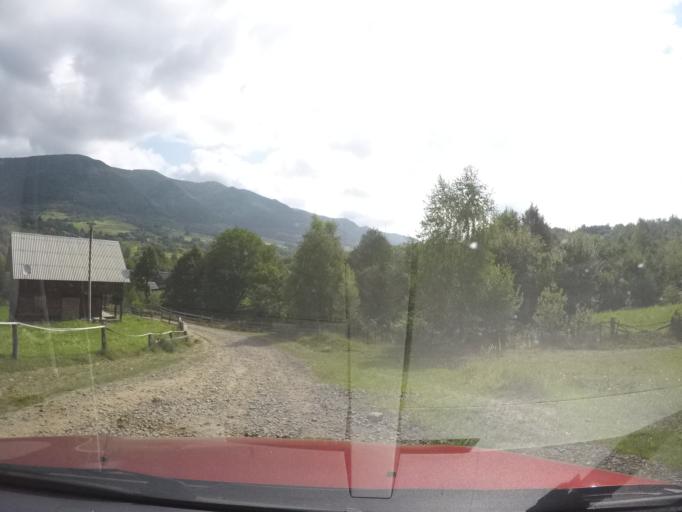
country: UA
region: Zakarpattia
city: Velykyi Bereznyi
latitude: 48.9447
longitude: 22.6754
